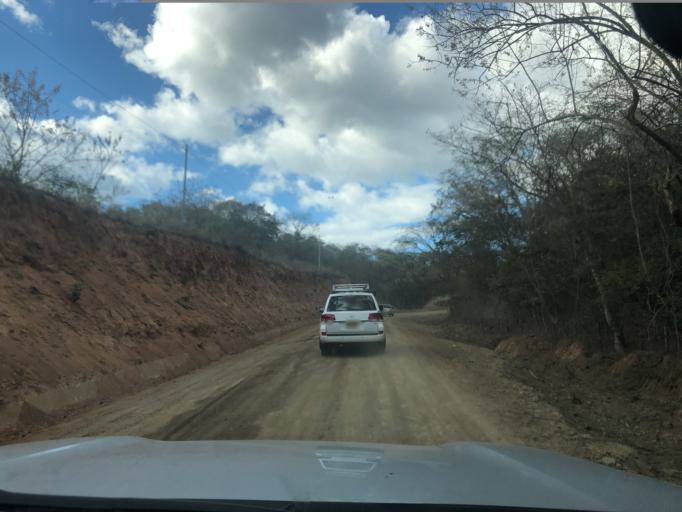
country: NI
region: Nueva Segovia
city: Ocotal
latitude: 13.6563
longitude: -86.6150
